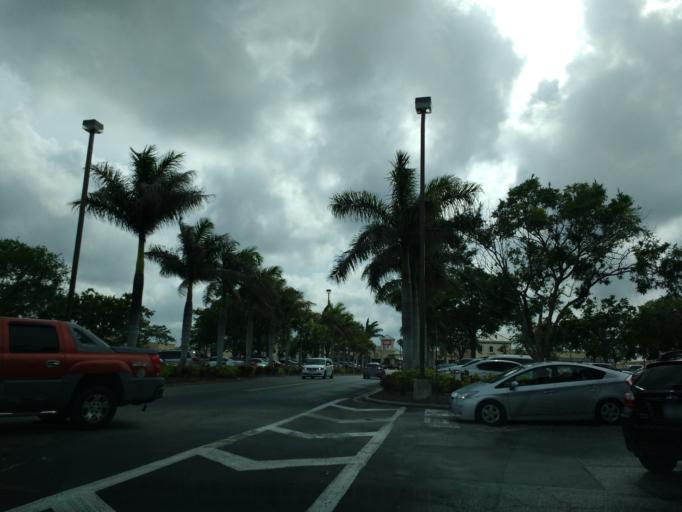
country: US
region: Florida
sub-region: Manatee County
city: Ellenton
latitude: 27.5343
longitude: -82.5053
